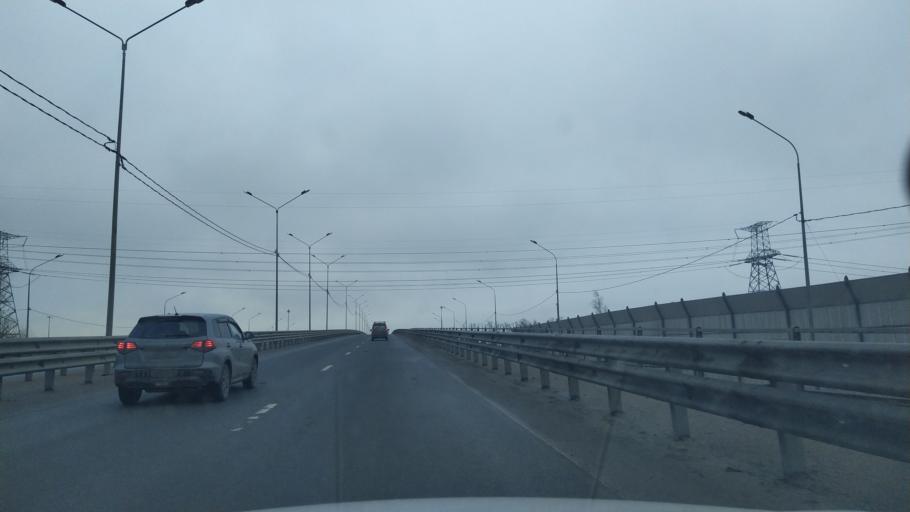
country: RU
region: St.-Petersburg
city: Aleksandrovskaya
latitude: 59.7197
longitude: 30.2777
